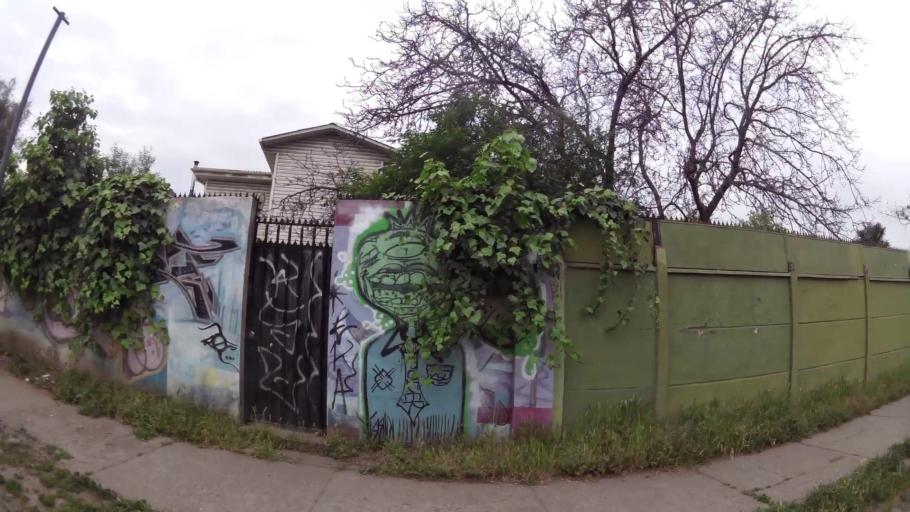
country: CL
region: Santiago Metropolitan
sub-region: Provincia de Santiago
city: Villa Presidente Frei, Nunoa, Santiago, Chile
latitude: -33.4832
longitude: -70.5889
